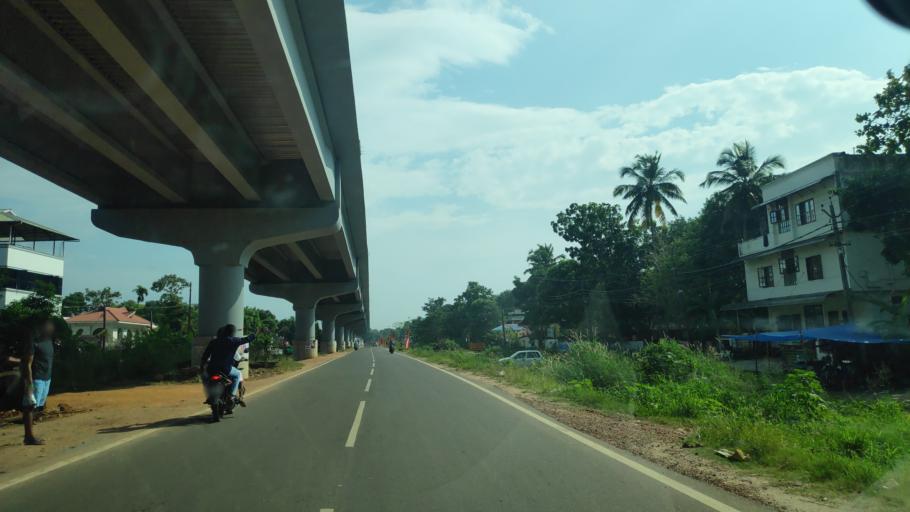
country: IN
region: Kerala
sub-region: Alappuzha
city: Alleppey
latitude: 9.4798
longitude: 76.3219
